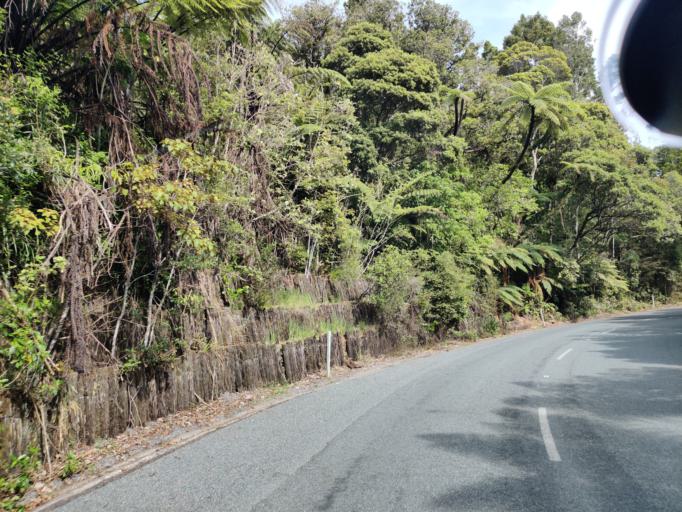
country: NZ
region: Northland
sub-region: Kaipara District
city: Dargaville
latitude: -35.6465
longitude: 173.5599
